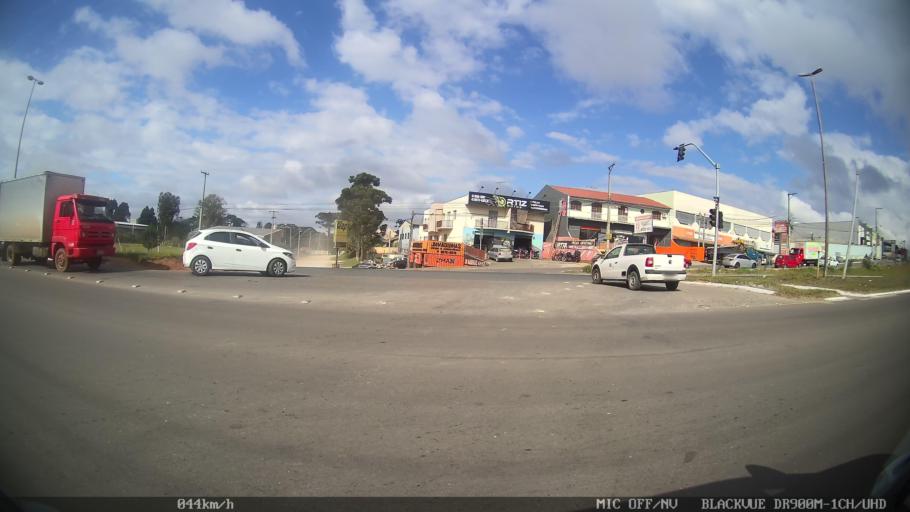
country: BR
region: Parana
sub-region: Colombo
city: Colombo
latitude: -25.3520
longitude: -49.1791
